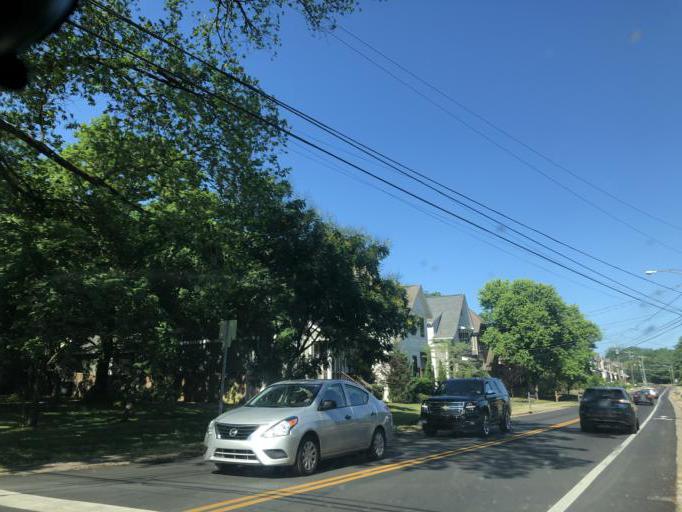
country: US
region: Tennessee
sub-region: Davidson County
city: Oak Hill
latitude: 36.1074
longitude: -86.8008
